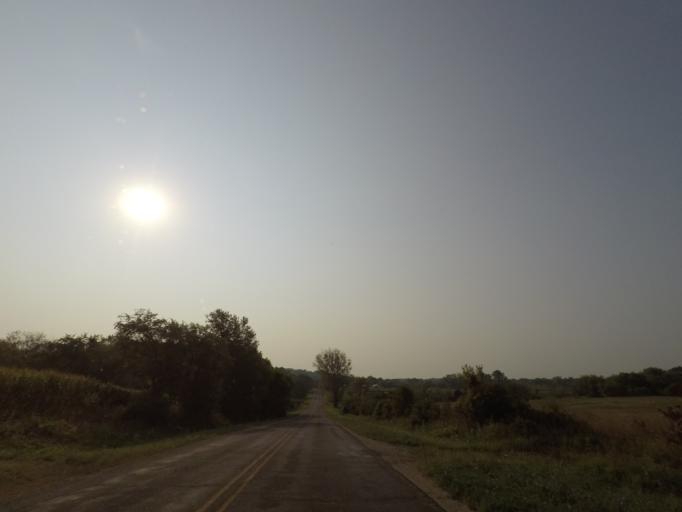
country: US
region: Wisconsin
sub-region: Dane County
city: Cottage Grove
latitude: 43.0456
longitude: -89.2356
